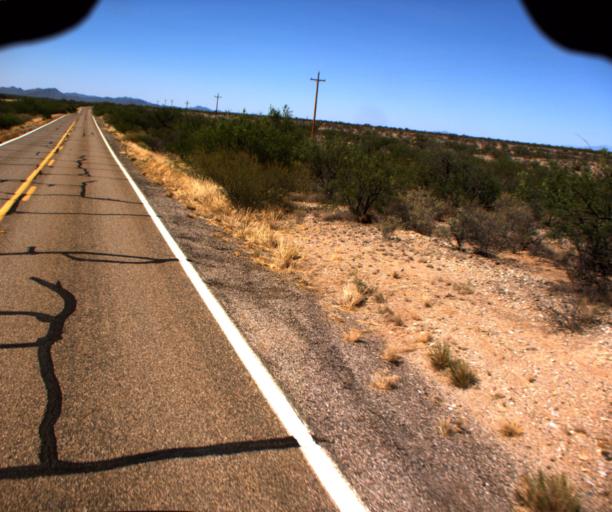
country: US
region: Arizona
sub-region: Pima County
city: Three Points
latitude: 31.9313
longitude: -111.3909
